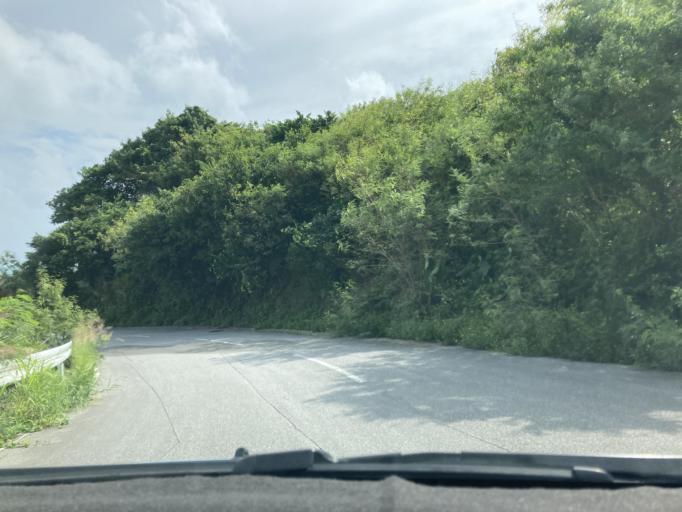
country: JP
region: Okinawa
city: Ginowan
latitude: 26.1532
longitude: 127.8034
